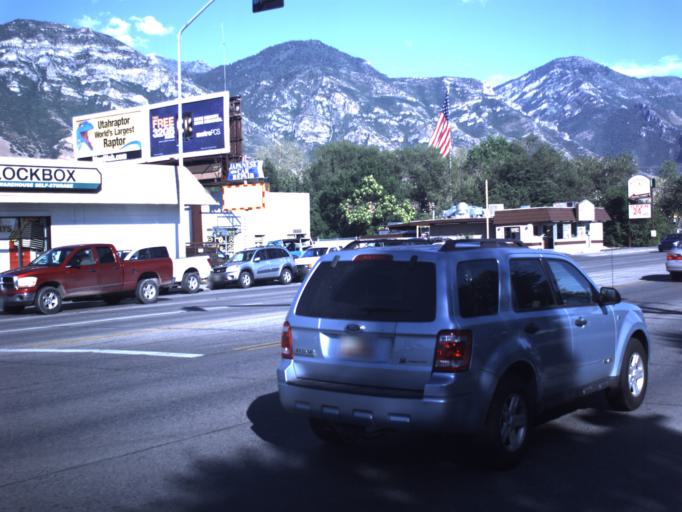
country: US
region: Utah
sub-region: Utah County
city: Provo
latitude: 40.2535
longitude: -111.6699
